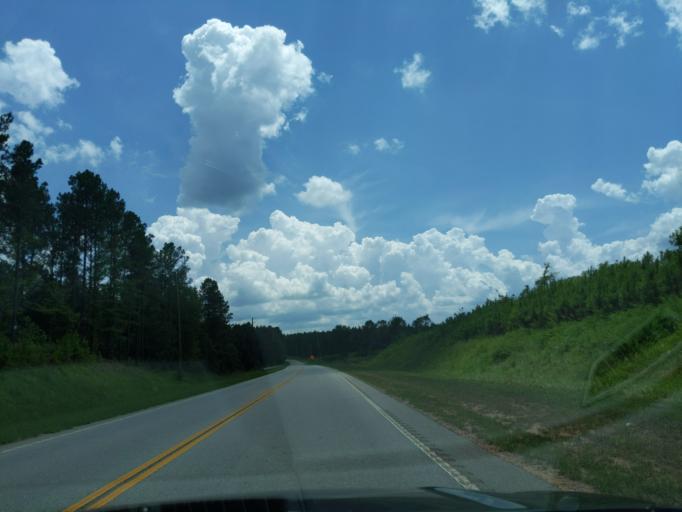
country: US
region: South Carolina
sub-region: Edgefield County
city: Edgefield
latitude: 33.8871
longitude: -82.0227
